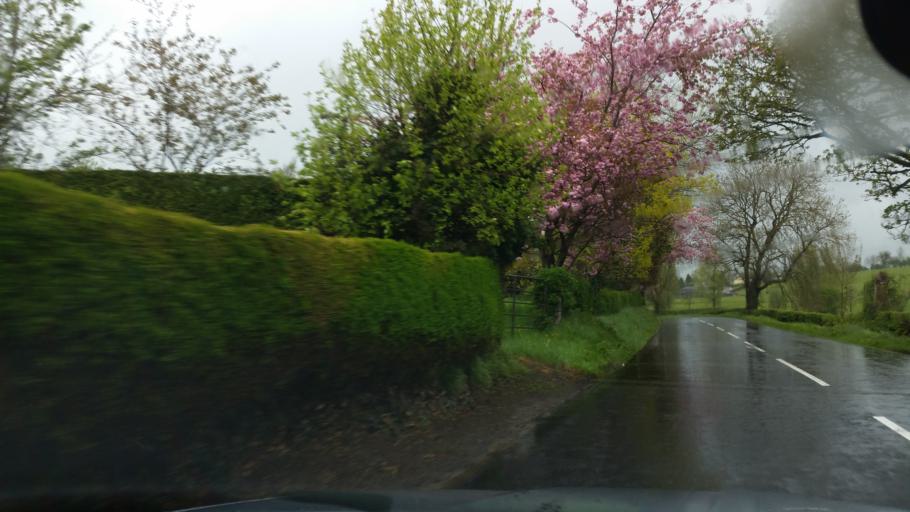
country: GB
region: Northern Ireland
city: Fintona
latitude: 54.5262
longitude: -7.2950
